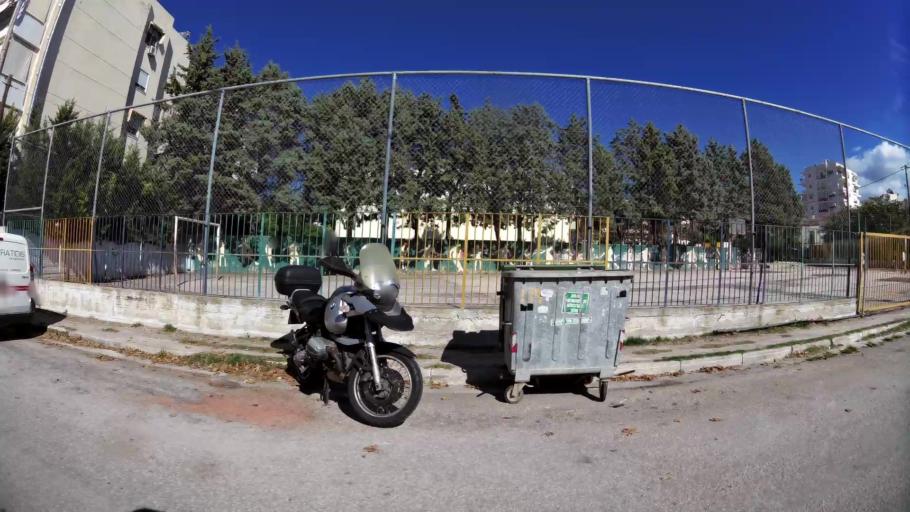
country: GR
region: Attica
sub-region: Nomarchia Anatolikis Attikis
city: Markopoulo
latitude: 37.8797
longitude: 23.9311
